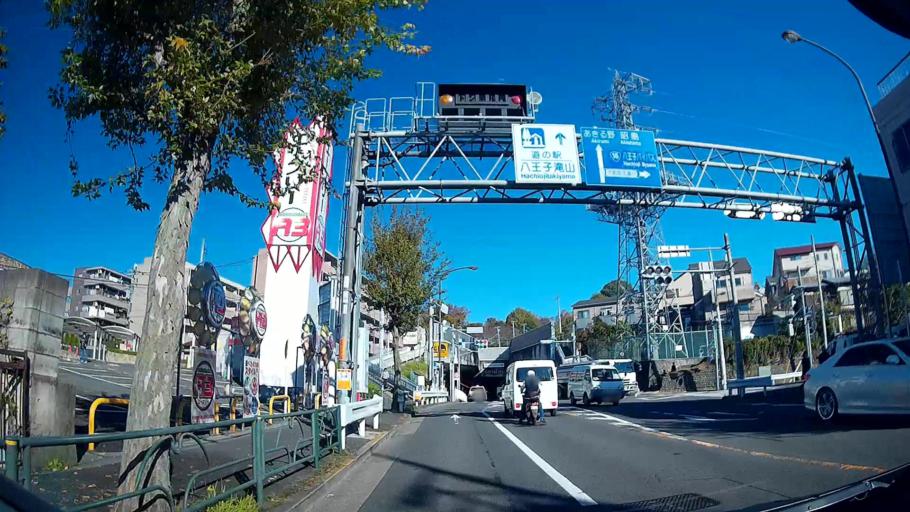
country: JP
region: Tokyo
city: Hachioji
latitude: 35.6676
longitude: 139.3411
